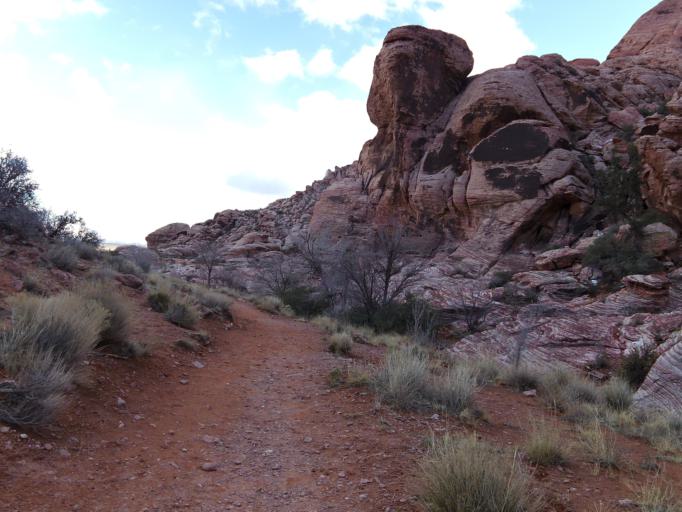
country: US
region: Nevada
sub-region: Clark County
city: Summerlin South
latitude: 36.1509
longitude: -115.4267
